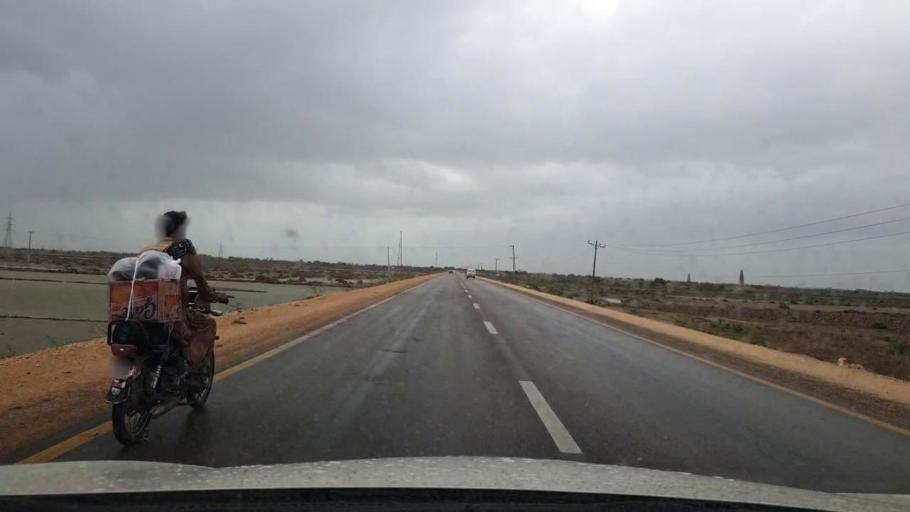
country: PK
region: Sindh
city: Kario
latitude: 24.6526
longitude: 68.6435
